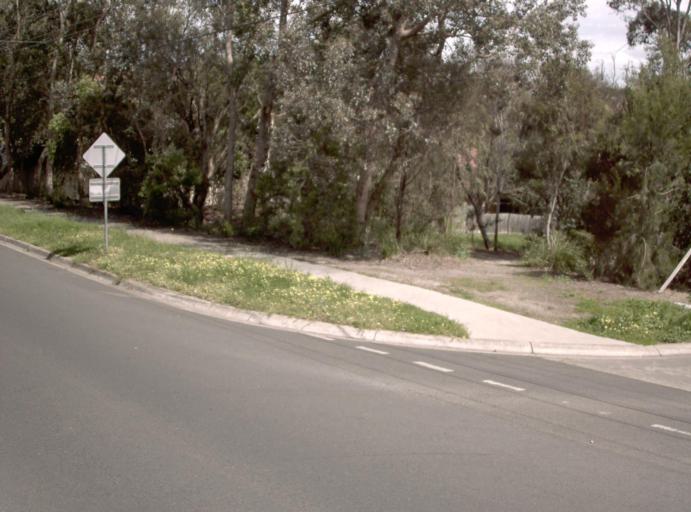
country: AU
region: Victoria
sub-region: Maroondah
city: Warranwood
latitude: -37.7690
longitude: 145.2461
